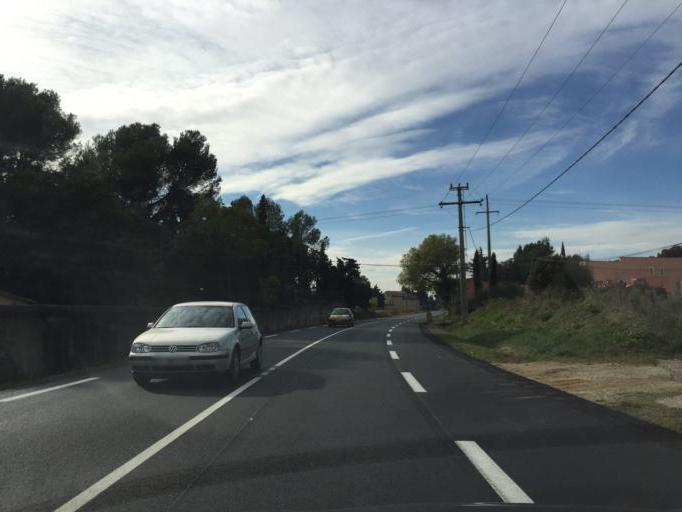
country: FR
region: Provence-Alpes-Cote d'Azur
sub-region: Departement du Vaucluse
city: Orange
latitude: 44.1677
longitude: 4.8095
